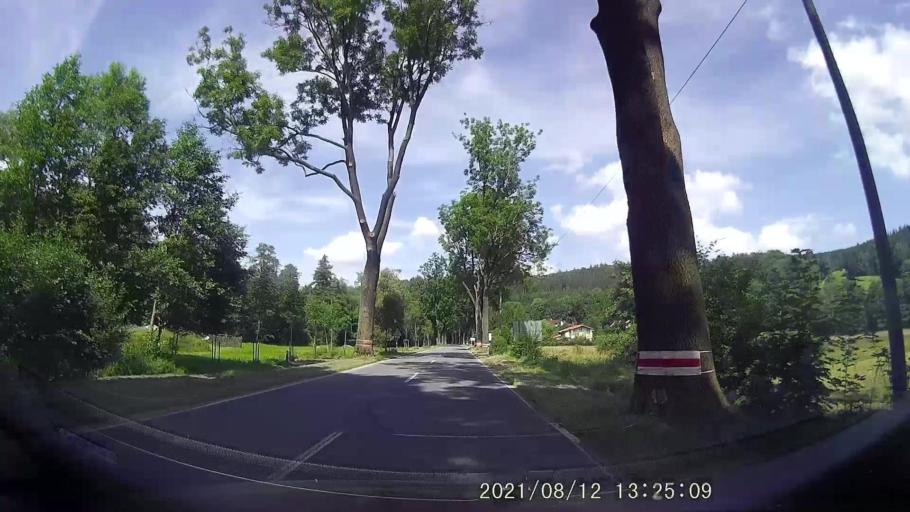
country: PL
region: Lower Silesian Voivodeship
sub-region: Powiat klodzki
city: Ladek-Zdroj
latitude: 50.3189
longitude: 16.8877
